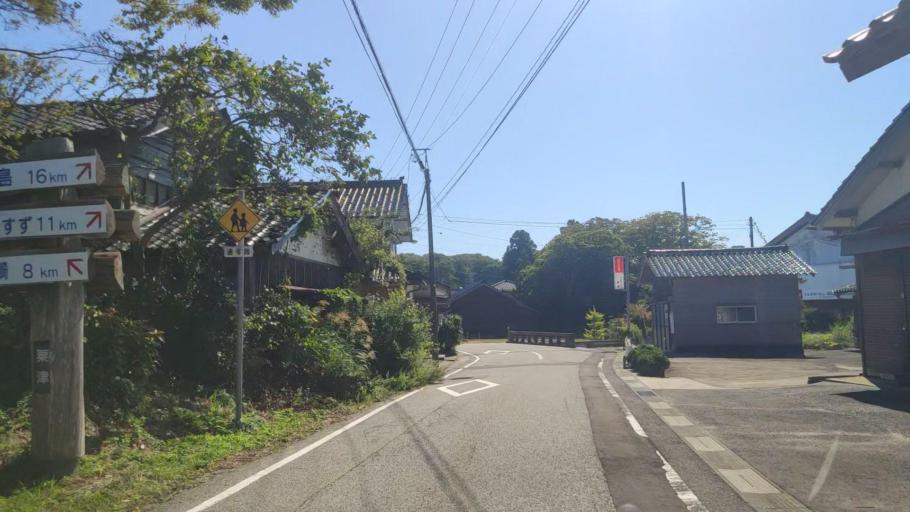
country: JP
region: Toyama
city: Nyuzen
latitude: 37.4831
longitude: 137.3391
